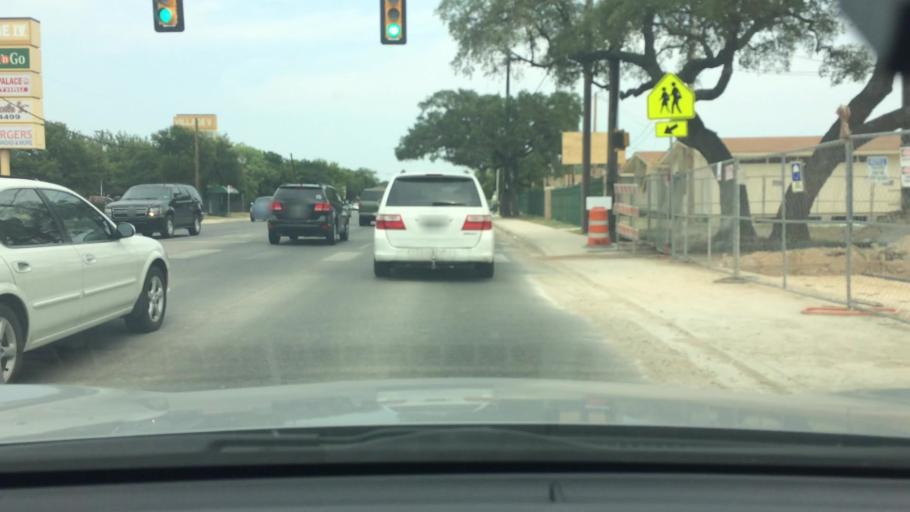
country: US
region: Texas
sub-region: Bexar County
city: Leon Valley
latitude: 29.4663
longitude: -98.6164
